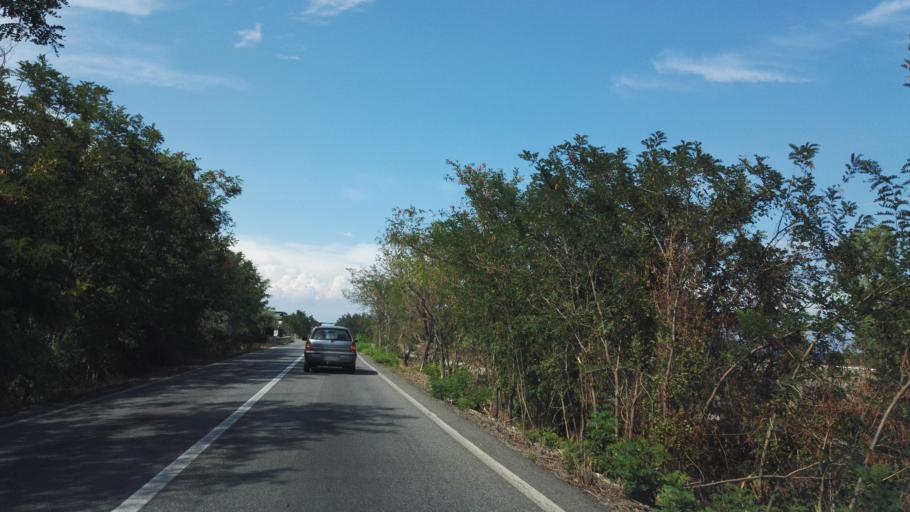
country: IT
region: Calabria
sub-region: Provincia di Catanzaro
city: Santa Caterina dello Ionio Marina
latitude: 38.5498
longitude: 16.5702
